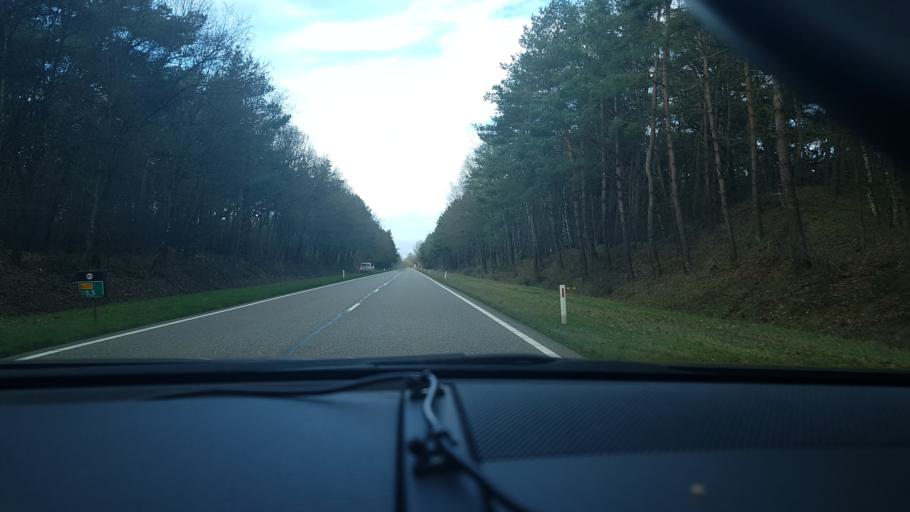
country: NL
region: Limburg
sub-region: Gemeente Peel en Maas
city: Maasbree
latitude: 51.3213
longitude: 6.0448
